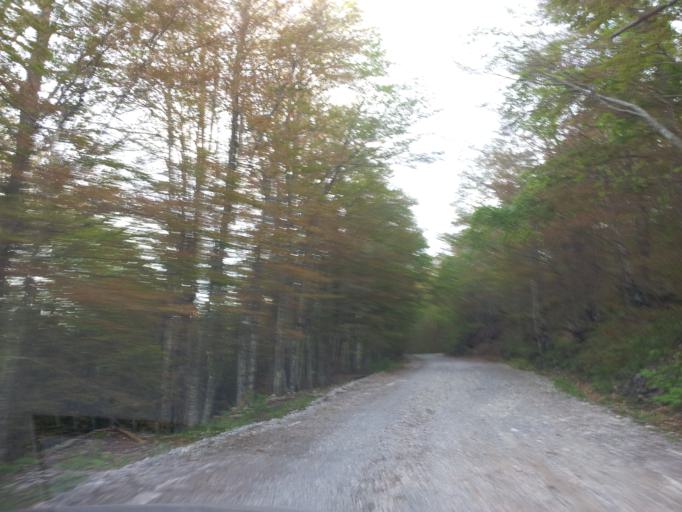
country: HR
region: Zadarska
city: Obrovac
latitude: 44.2962
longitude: 15.6511
